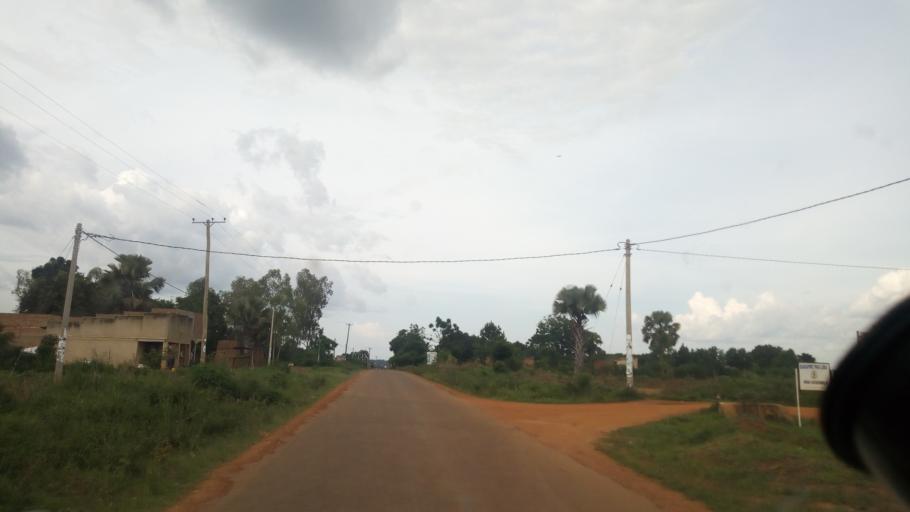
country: UG
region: Northern Region
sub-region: Lira District
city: Lira
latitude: 2.2557
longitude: 32.8479
